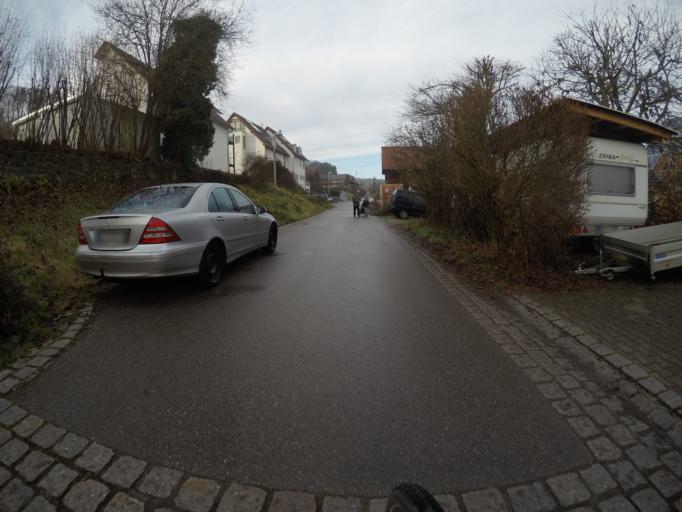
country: DE
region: Baden-Wuerttemberg
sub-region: Karlsruhe Region
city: Gechingen
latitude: 48.6772
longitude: 8.8500
